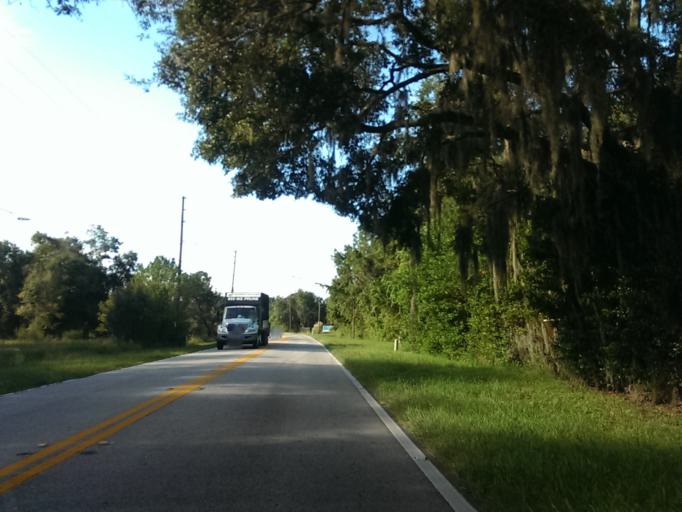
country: US
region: Florida
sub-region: Polk County
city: Citrus Ridge
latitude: 28.3555
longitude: -81.6462
